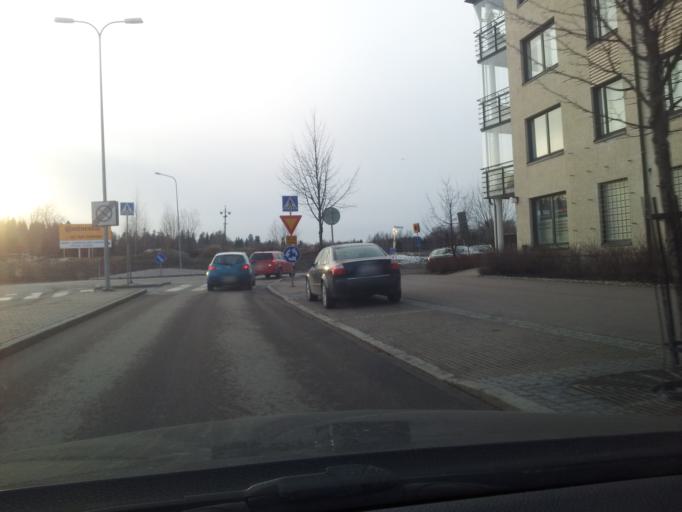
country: FI
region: Uusimaa
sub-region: Helsinki
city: Kilo
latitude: 60.2174
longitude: 24.8016
